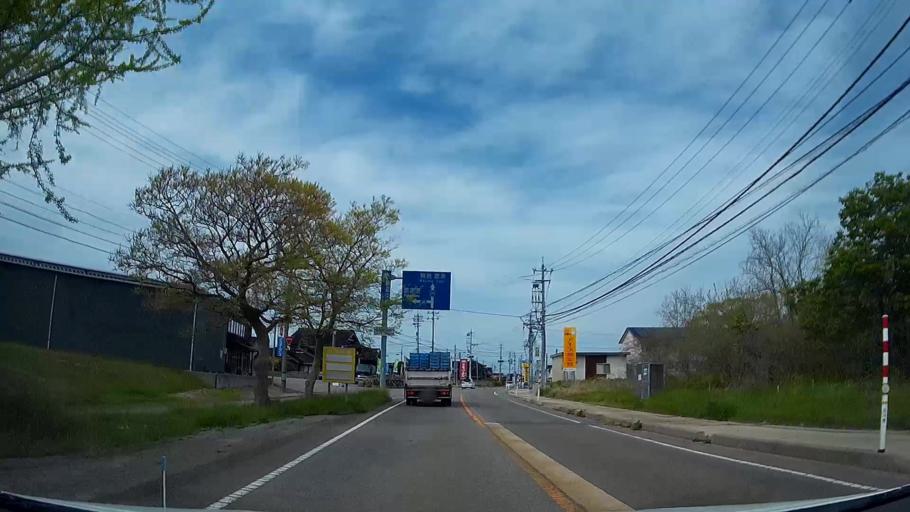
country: JP
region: Ishikawa
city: Hakui
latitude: 36.9955
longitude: 136.7767
